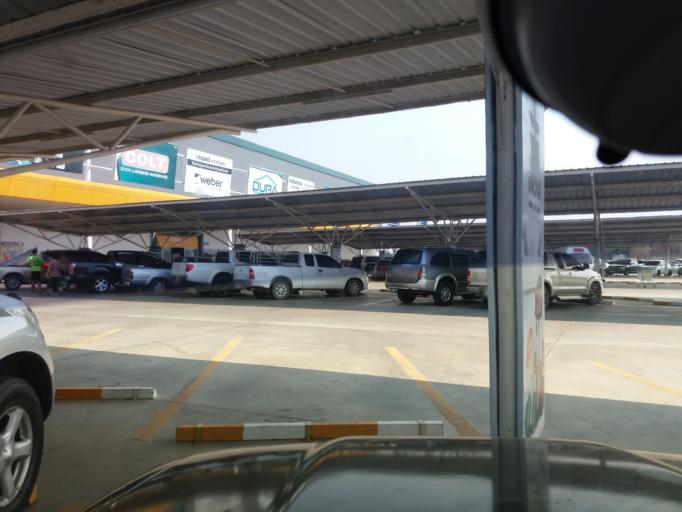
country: TH
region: Sing Buri
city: Sing Buri
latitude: 14.8735
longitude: 100.3975
